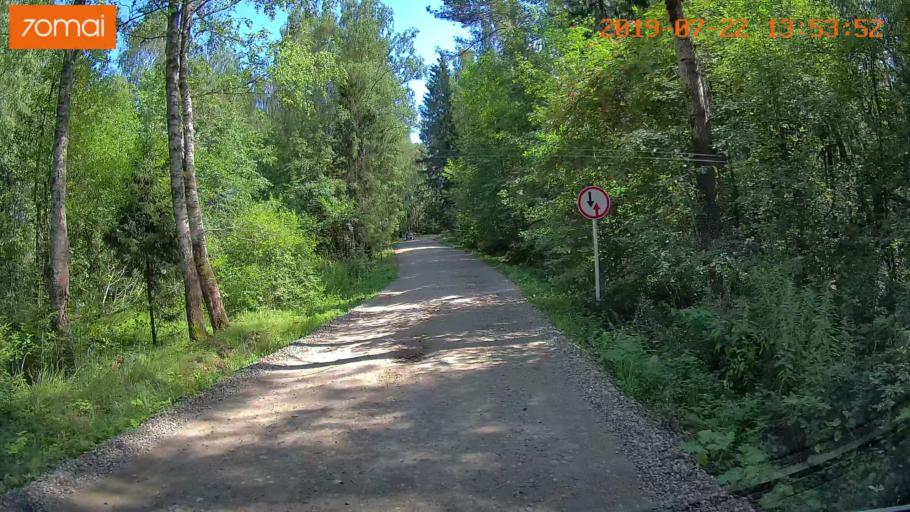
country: RU
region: Ivanovo
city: Novo-Talitsy
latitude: 57.0799
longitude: 40.8784
